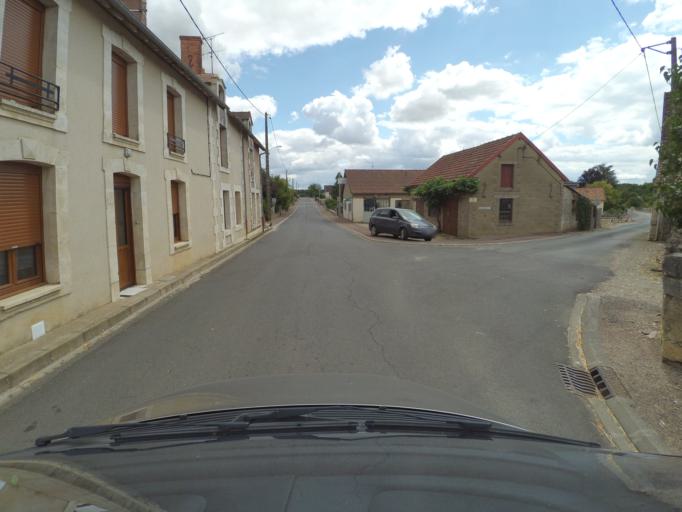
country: FR
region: Poitou-Charentes
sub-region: Departement de la Vienne
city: Saint-Savin
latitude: 46.5466
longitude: 0.9770
